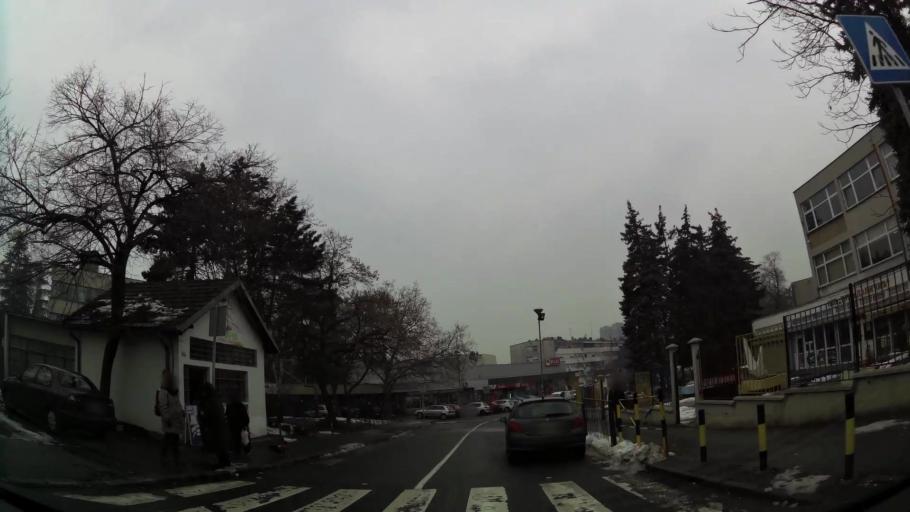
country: RS
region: Central Serbia
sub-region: Belgrade
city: Vozdovac
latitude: 44.7696
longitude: 20.4913
